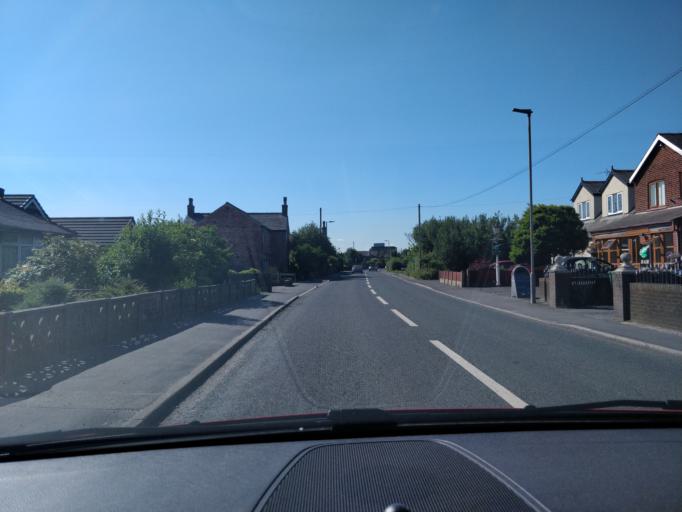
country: GB
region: England
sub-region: Lancashire
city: Tarleton
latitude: 53.6884
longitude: -2.8332
